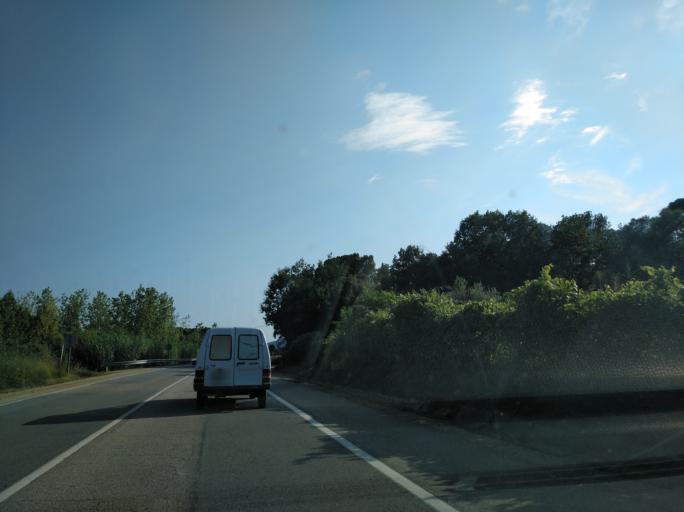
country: ES
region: Catalonia
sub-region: Provincia de Girona
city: Brunyola
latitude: 41.8767
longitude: 2.6946
